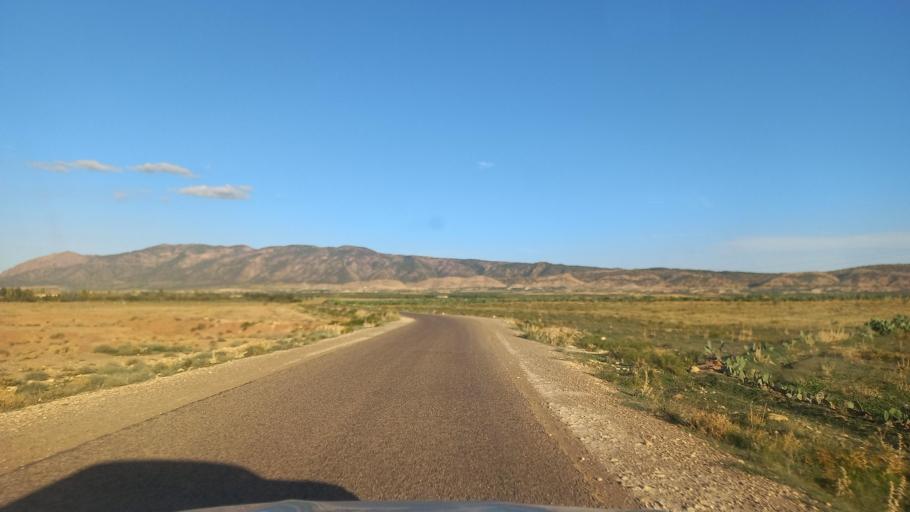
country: TN
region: Al Qasrayn
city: Sbiba
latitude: 35.4112
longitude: 9.1396
